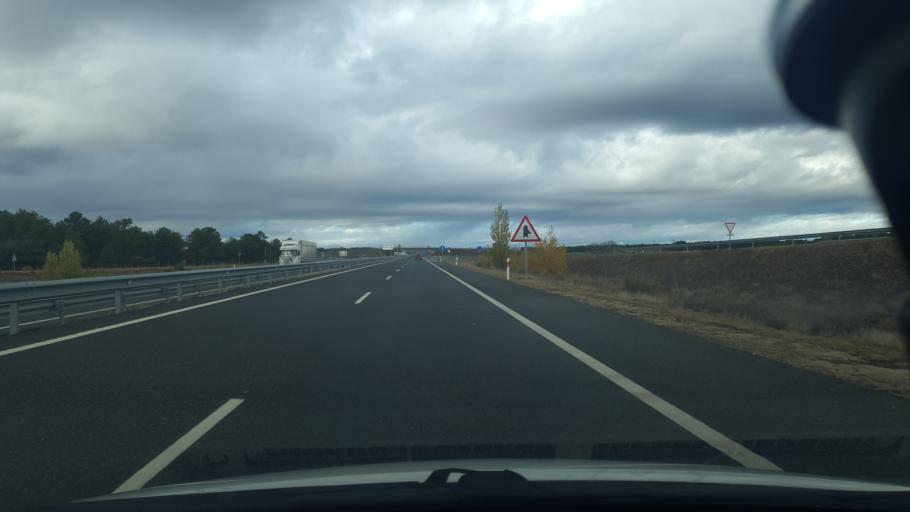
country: ES
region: Castille and Leon
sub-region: Provincia de Segovia
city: Sanchonuno
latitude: 41.2953
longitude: -4.3002
